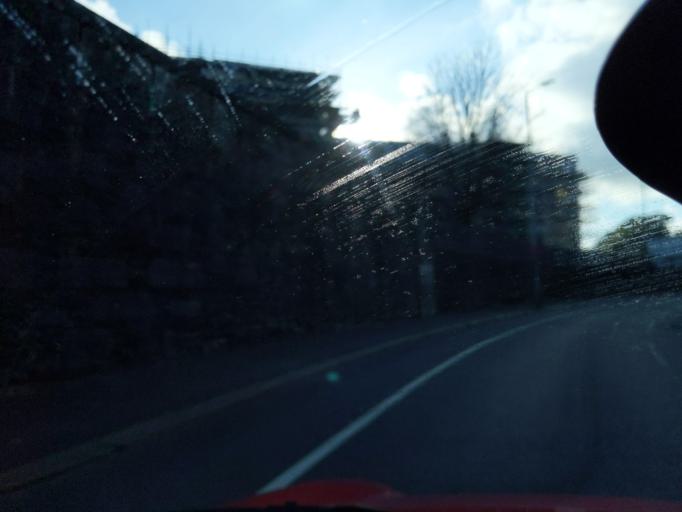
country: GB
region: England
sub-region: Cornwall
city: Millbrook
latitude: 50.3693
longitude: -4.1680
